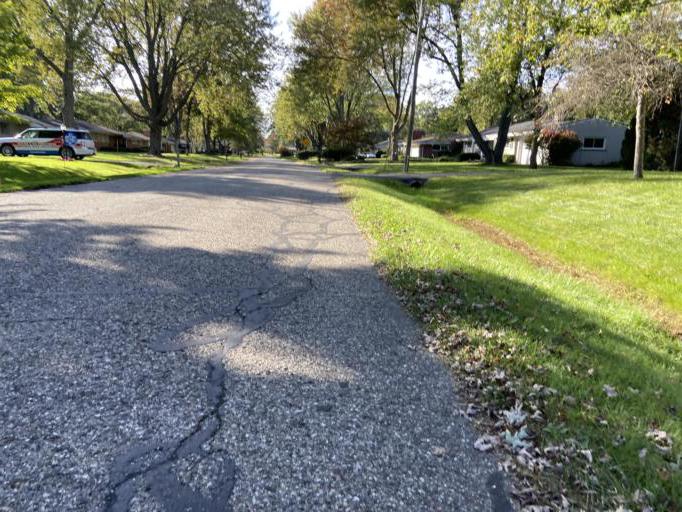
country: US
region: Michigan
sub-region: Oakland County
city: Farmington Hills
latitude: 42.5015
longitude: -83.3713
